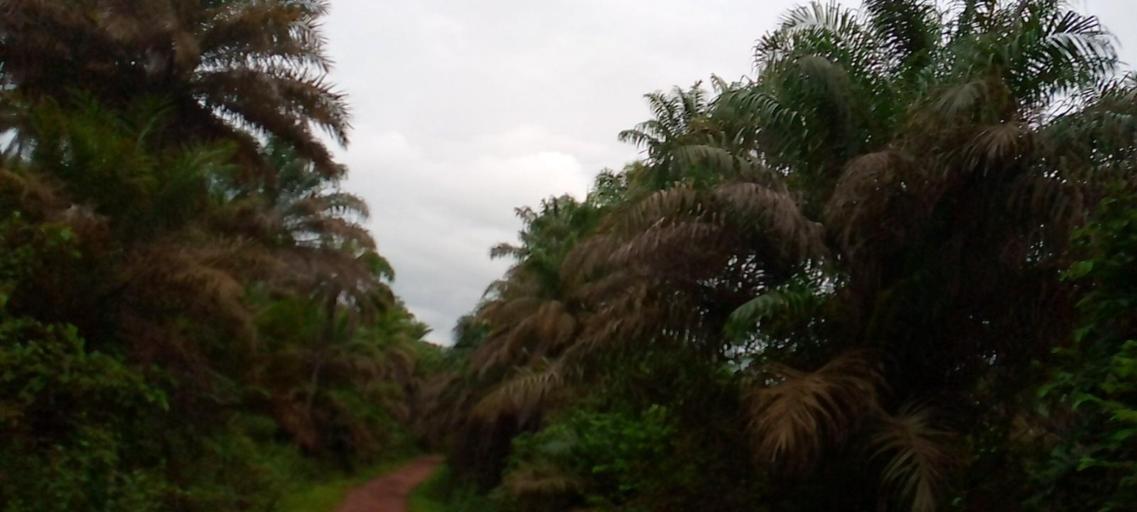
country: SL
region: Northern Province
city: Port Loko
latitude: 8.7187
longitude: -12.8025
